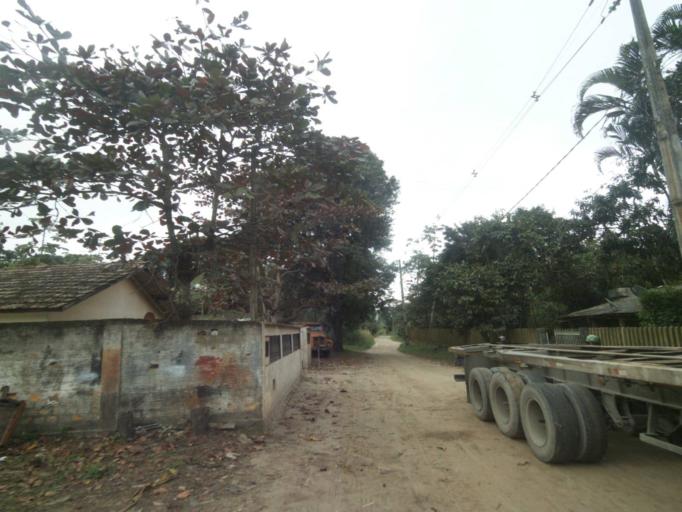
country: BR
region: Parana
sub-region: Paranagua
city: Paranagua
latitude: -25.5411
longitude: -48.5541
